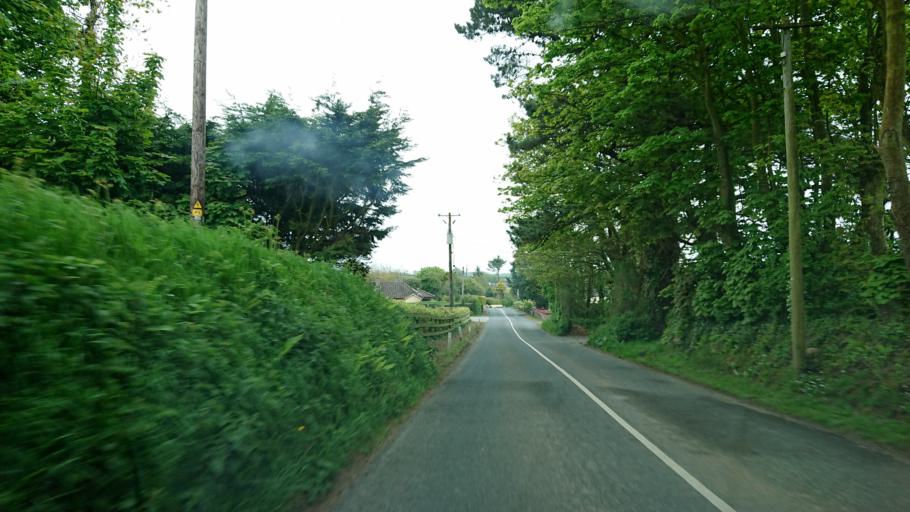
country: IE
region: Munster
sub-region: Waterford
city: Waterford
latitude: 52.2178
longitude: -7.0437
